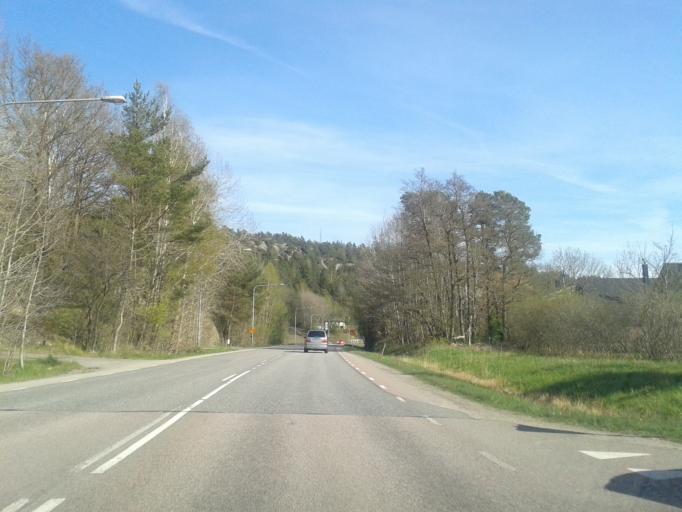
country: SE
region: Vaestra Goetaland
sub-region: Ale Kommun
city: Nodinge-Nol
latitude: 57.8974
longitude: 12.0635
